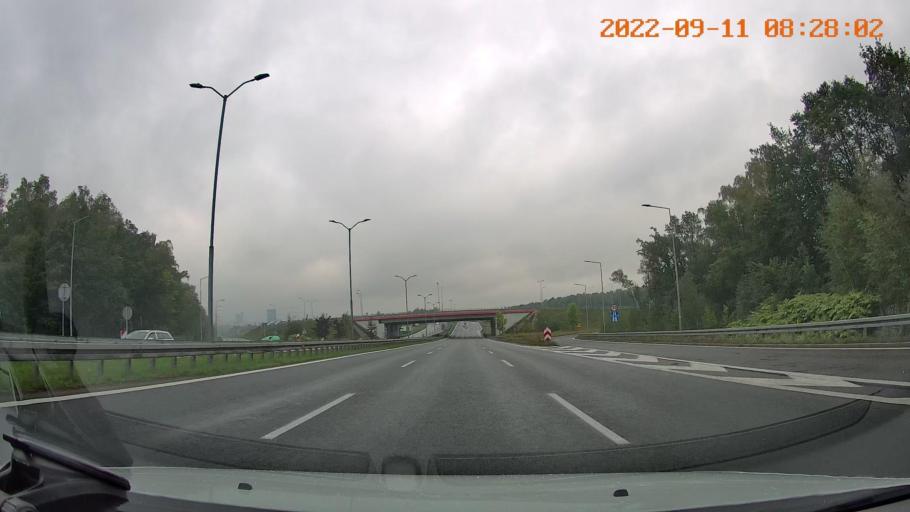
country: PL
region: Silesian Voivodeship
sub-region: Katowice
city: Katowice
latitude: 50.2380
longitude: 19.0536
